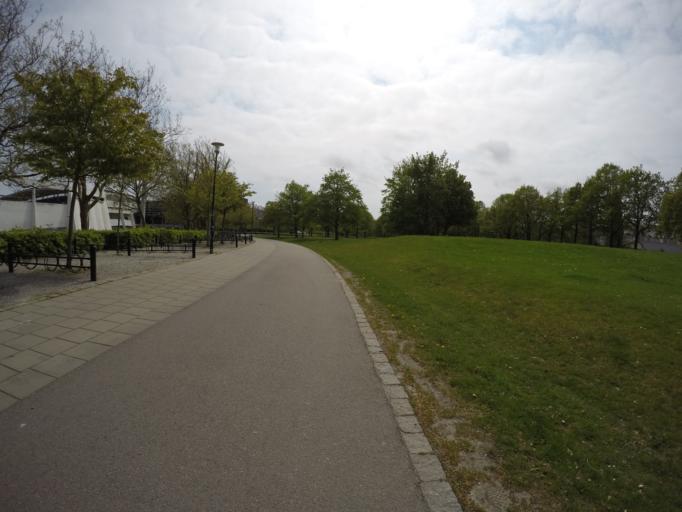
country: SE
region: Skane
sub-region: Malmo
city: Malmoe
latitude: 55.5866
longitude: 12.9869
